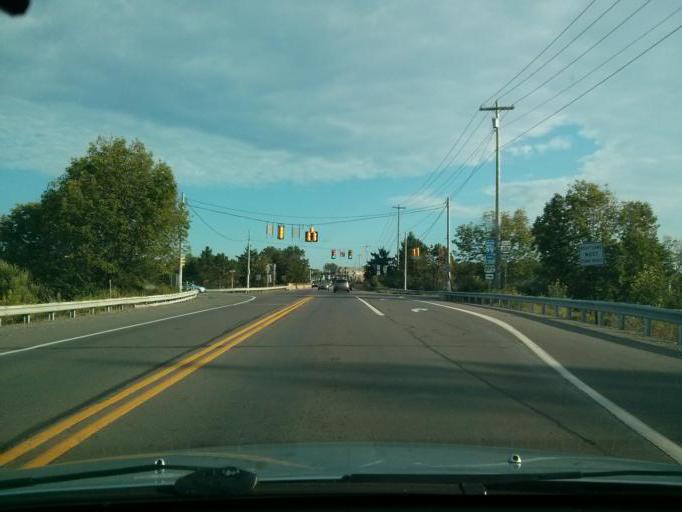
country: US
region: Pennsylvania
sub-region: Centre County
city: Park Forest Village
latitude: 40.8205
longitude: -77.9013
